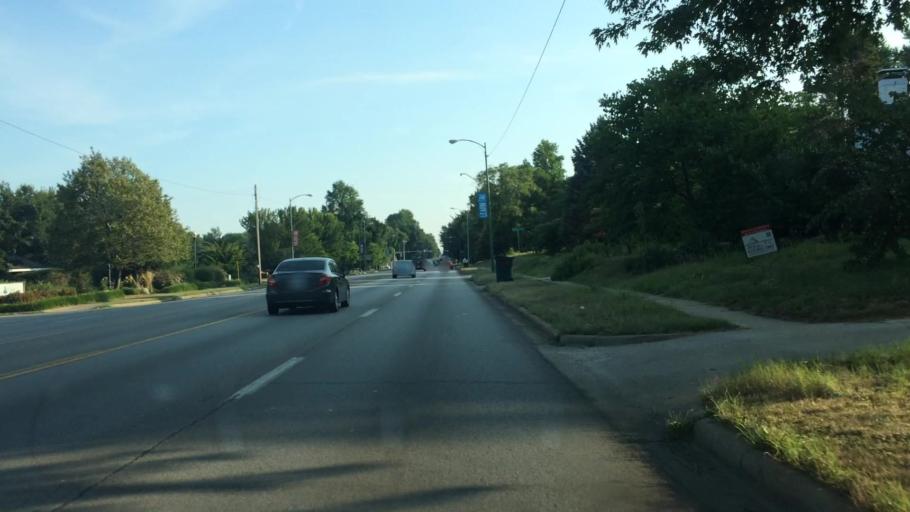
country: US
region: Missouri
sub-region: Greene County
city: Springfield
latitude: 37.1862
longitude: -93.2765
